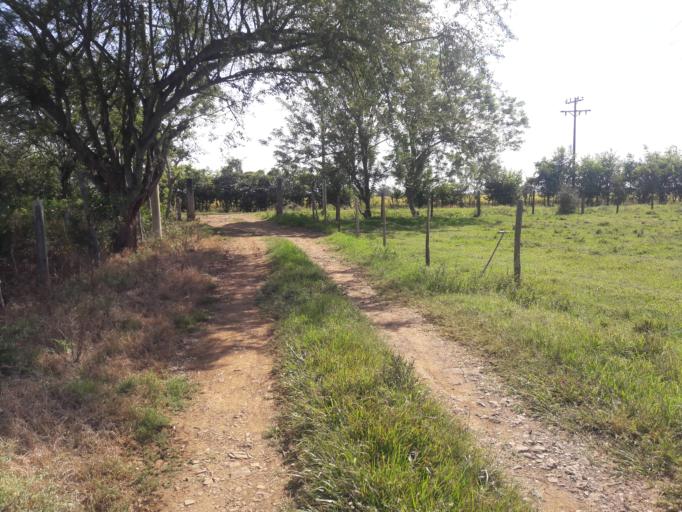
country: CO
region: Valle del Cauca
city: Jamundi
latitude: 3.2974
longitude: -76.5103
